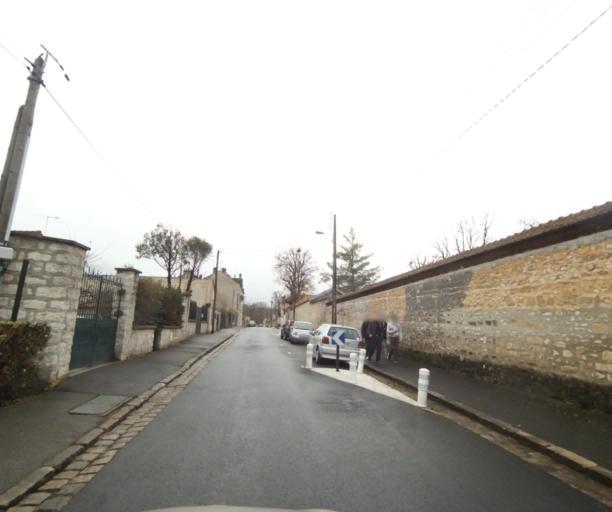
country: FR
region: Ile-de-France
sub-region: Departement de Seine-et-Marne
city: Avon
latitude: 48.4039
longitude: 2.7179
